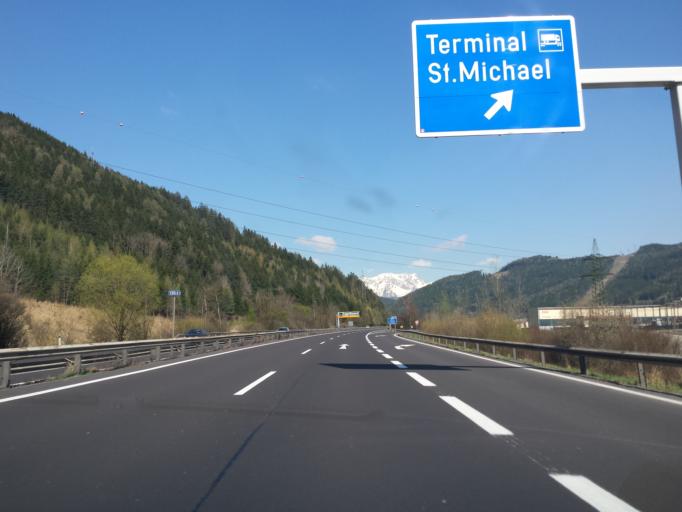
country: AT
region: Styria
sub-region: Politischer Bezirk Leoben
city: Sankt Michael in Obersteiermark
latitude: 47.3542
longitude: 15.0026
